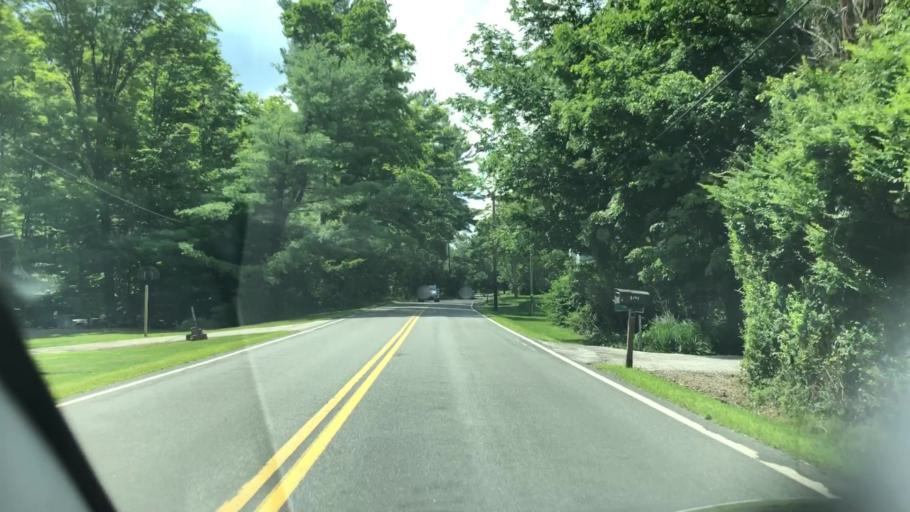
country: US
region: Ohio
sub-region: Summit County
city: Montrose-Ghent
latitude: 41.1598
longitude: -81.6458
